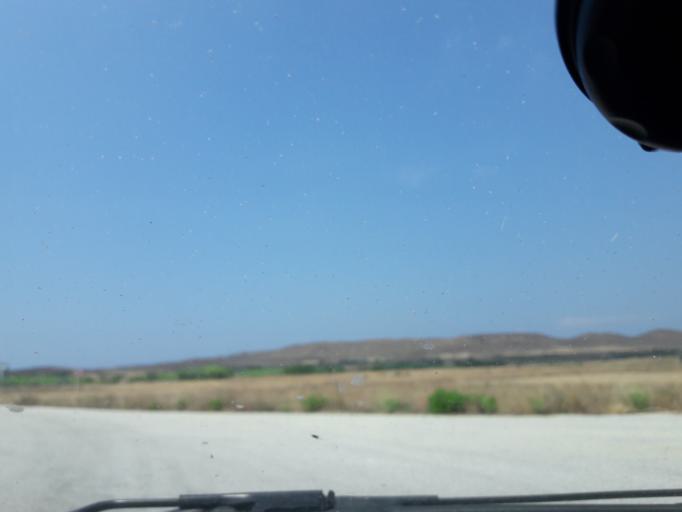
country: GR
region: North Aegean
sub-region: Nomos Lesvou
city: Myrina
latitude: 39.9620
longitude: 25.3703
